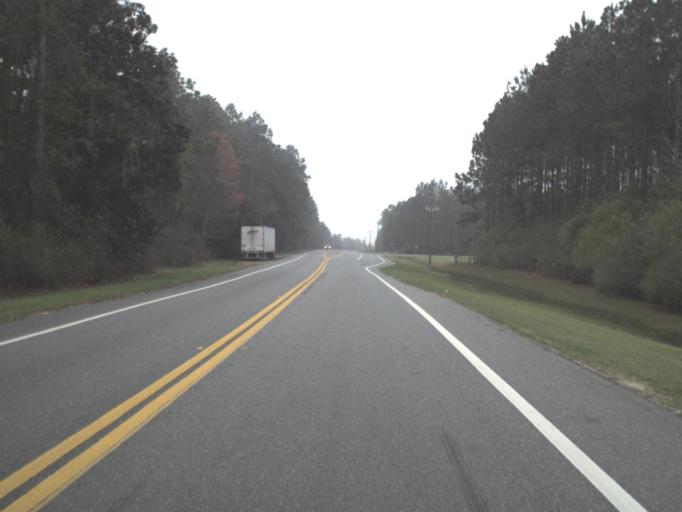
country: US
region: Florida
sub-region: Liberty County
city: Bristol
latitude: 30.4381
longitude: -84.7710
